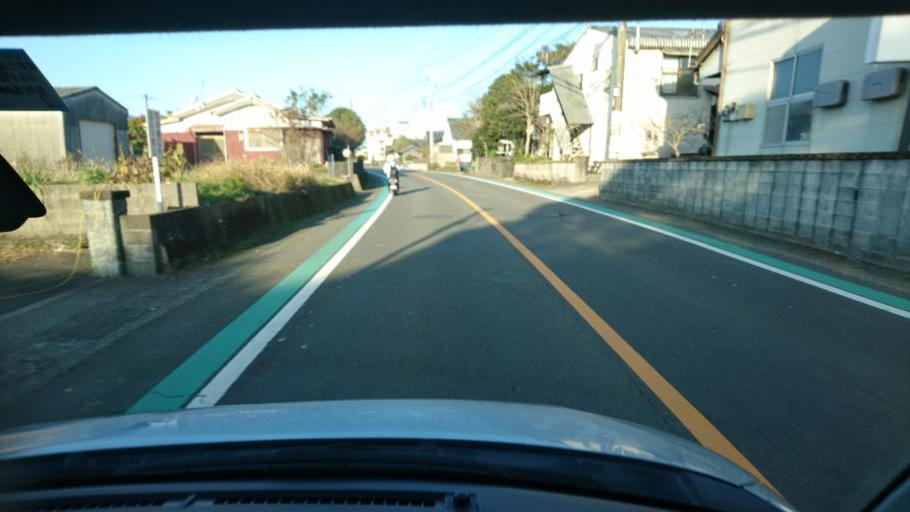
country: JP
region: Miyazaki
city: Miyazaki-shi
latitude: 31.8424
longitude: 131.4145
